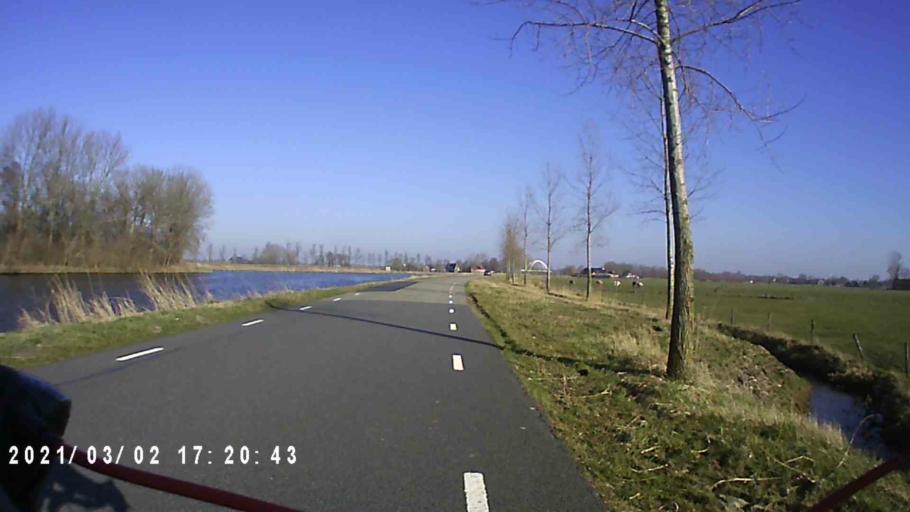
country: NL
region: Groningen
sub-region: Gemeente Zuidhorn
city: Noordhorn
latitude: 53.2538
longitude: 6.3710
